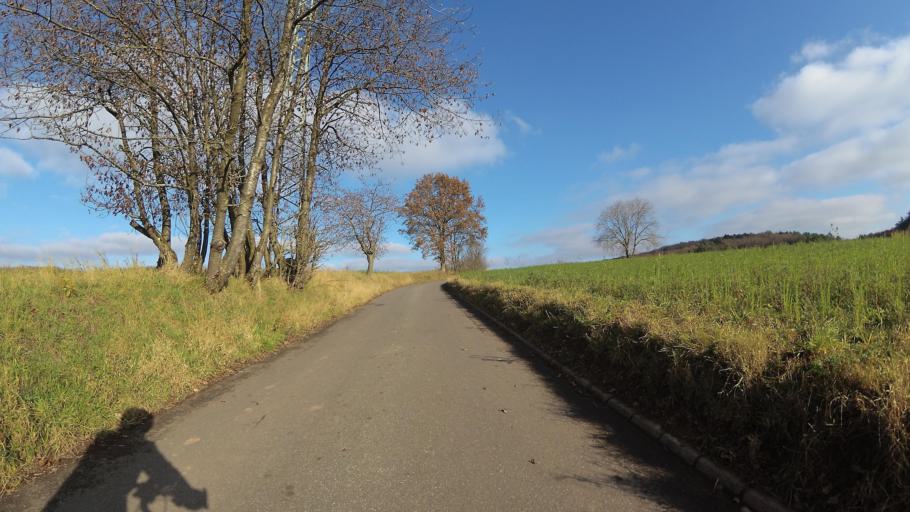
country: DE
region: Rheinland-Pfalz
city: Hahnweiler
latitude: 49.5324
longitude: 7.1872
